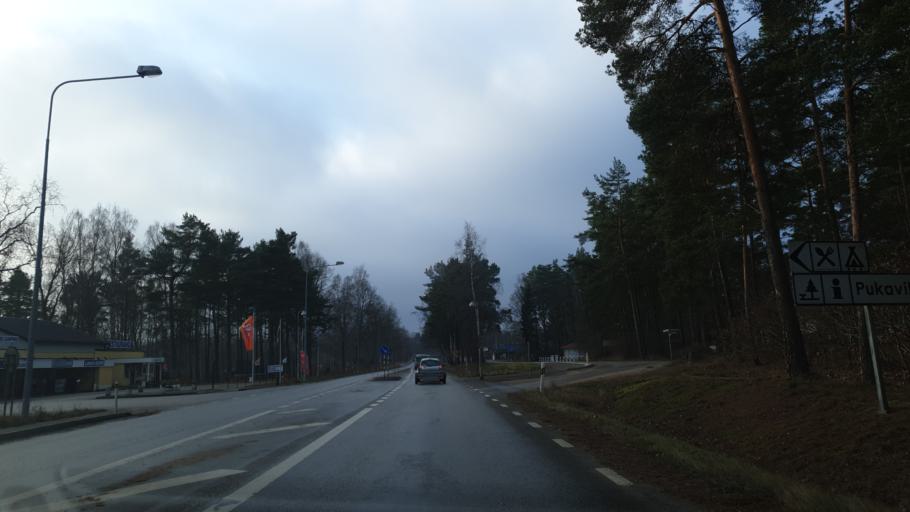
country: SE
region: Blekinge
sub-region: Karlshamns Kommun
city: Morrum
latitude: 56.1538
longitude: 14.6736
